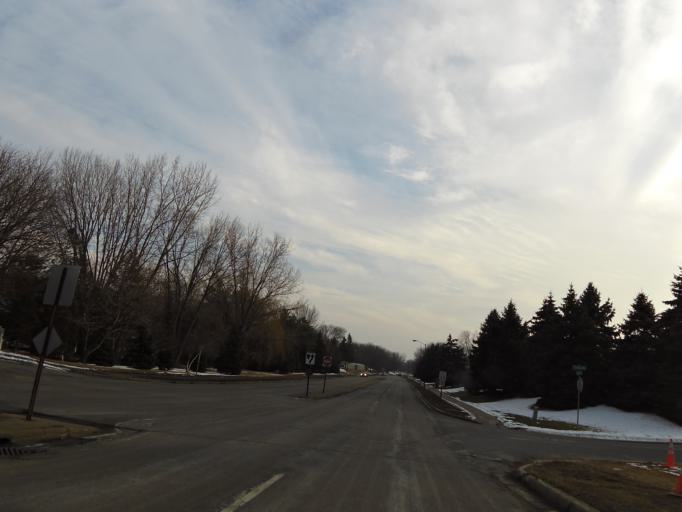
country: US
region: Minnesota
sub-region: Hennepin County
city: Eden Prairie
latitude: 44.8484
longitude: -93.4241
